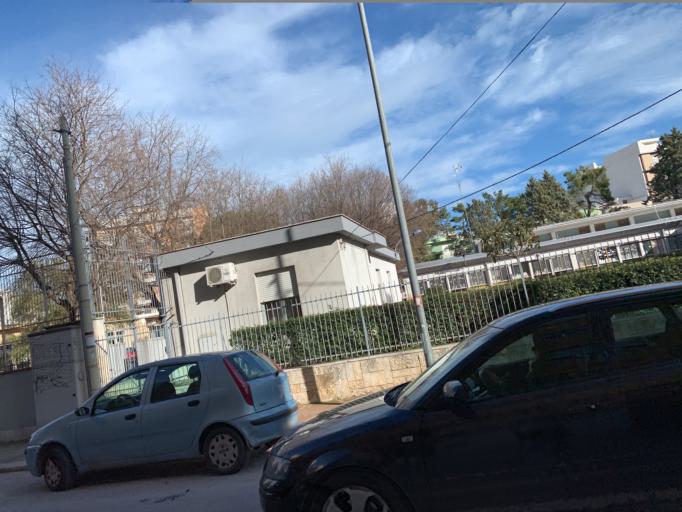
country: IT
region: Apulia
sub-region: Provincia di Barletta - Andria - Trani
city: Andria
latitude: 41.2317
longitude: 16.2970
